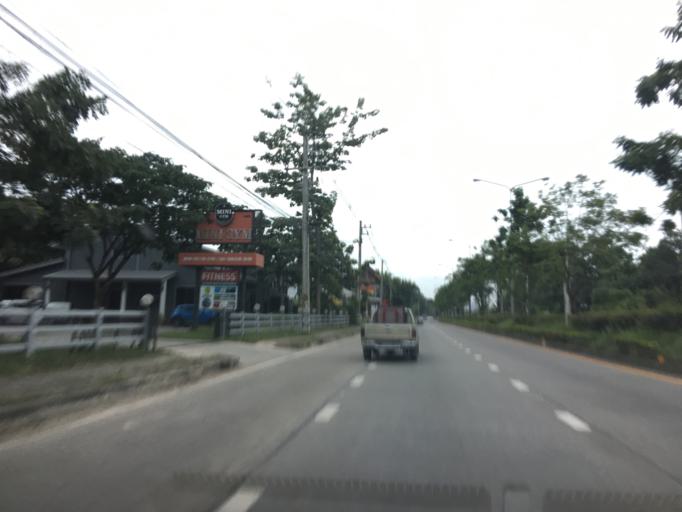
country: TH
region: Chiang Mai
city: San Sai
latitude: 18.8325
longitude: 99.0042
